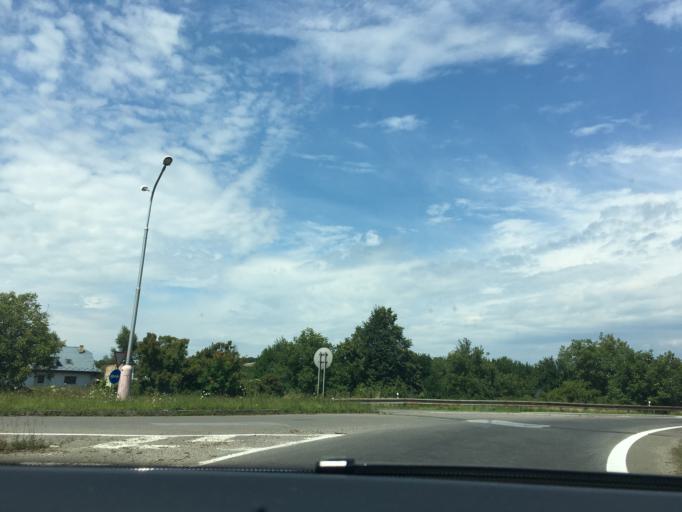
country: SK
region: Presovsky
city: Vranov nad Topl'ou
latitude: 48.8663
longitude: 21.7109
